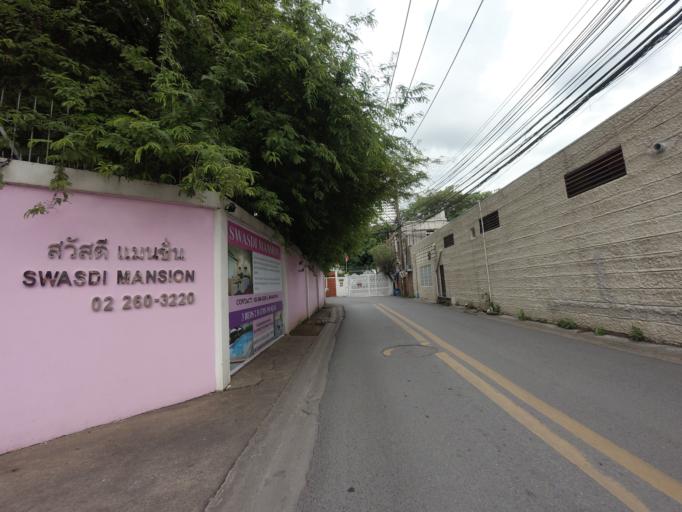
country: TH
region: Bangkok
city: Watthana
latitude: 13.7416
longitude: 100.5679
